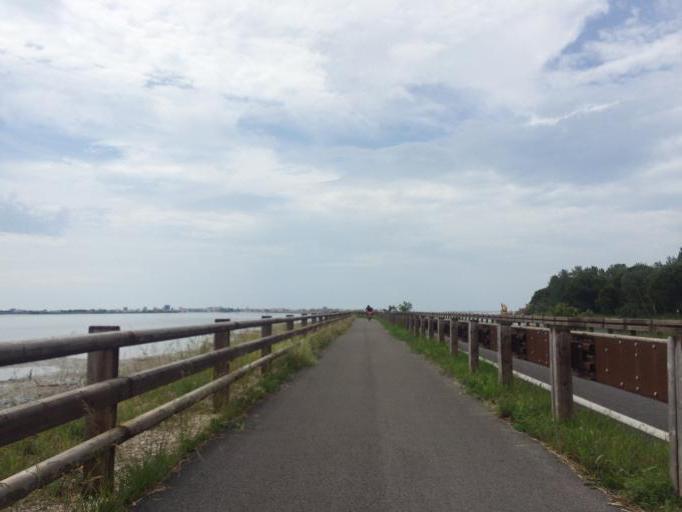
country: IT
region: Friuli Venezia Giulia
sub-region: Provincia di Gorizia
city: Grado
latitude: 45.7113
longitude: 13.3836
